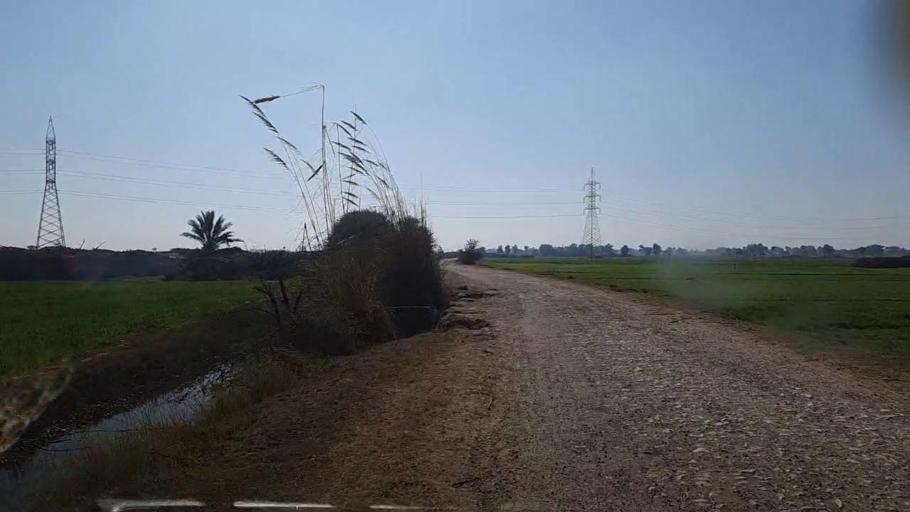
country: PK
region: Sindh
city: Khairpur
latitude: 28.0415
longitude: 69.7827
